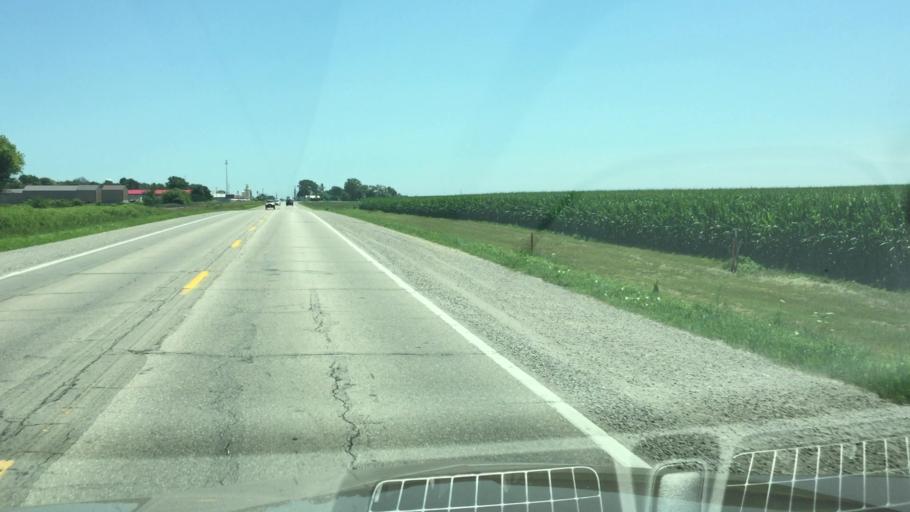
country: US
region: Iowa
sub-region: Cedar County
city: Mechanicsville
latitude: 41.9050
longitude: -91.2665
